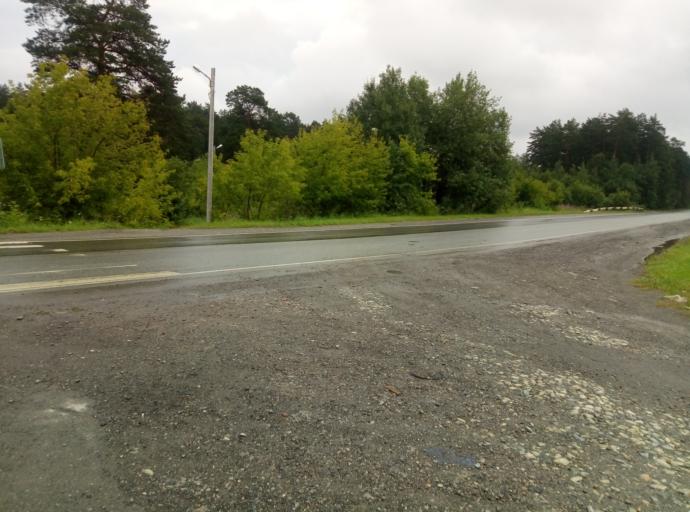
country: RU
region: Sverdlovsk
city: Beryozovsky
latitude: 56.9006
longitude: 60.7568
